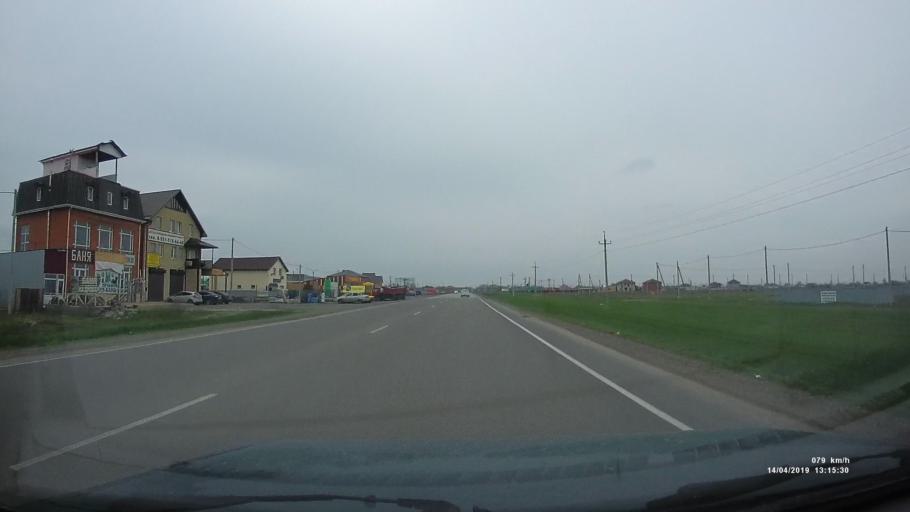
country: RU
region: Rostov
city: Kuleshovka
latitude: 47.0837
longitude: 39.5942
